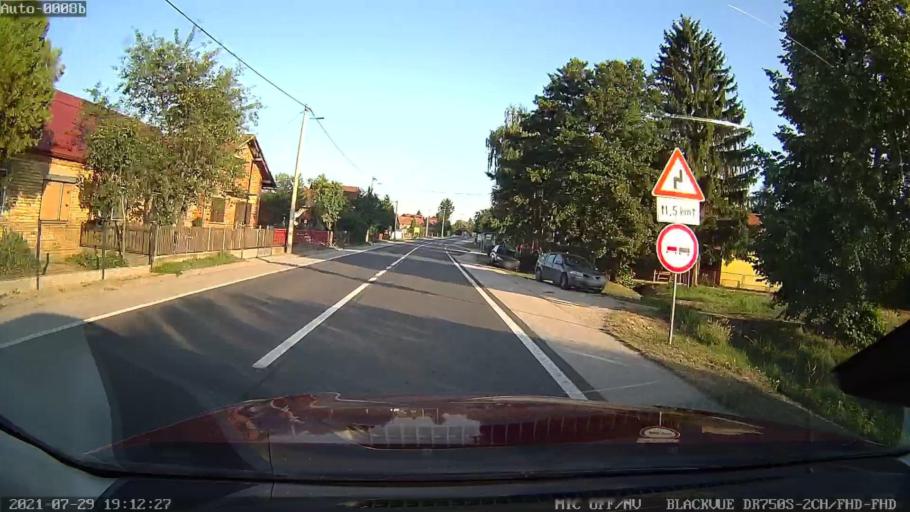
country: HR
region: Varazdinska
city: Jalzabet
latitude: 46.2674
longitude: 16.5164
